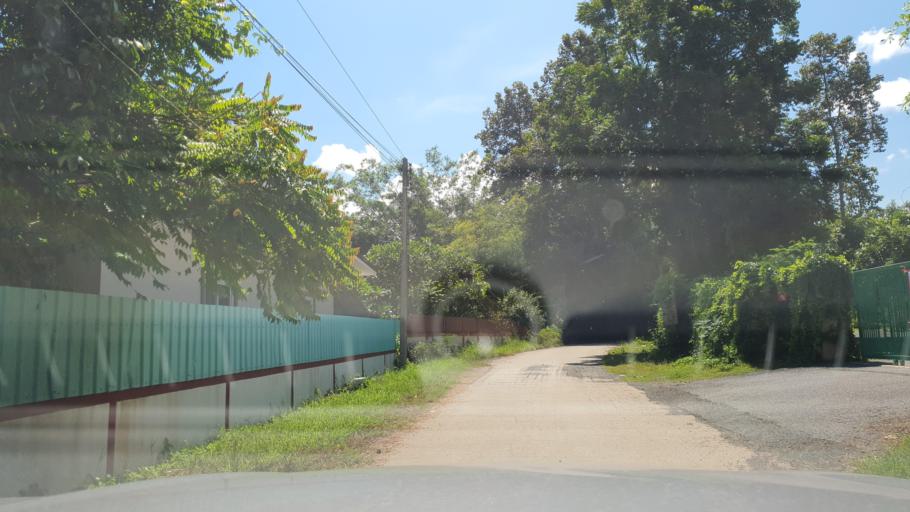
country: TH
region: Chiang Mai
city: Mae On
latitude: 18.7780
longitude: 99.1827
